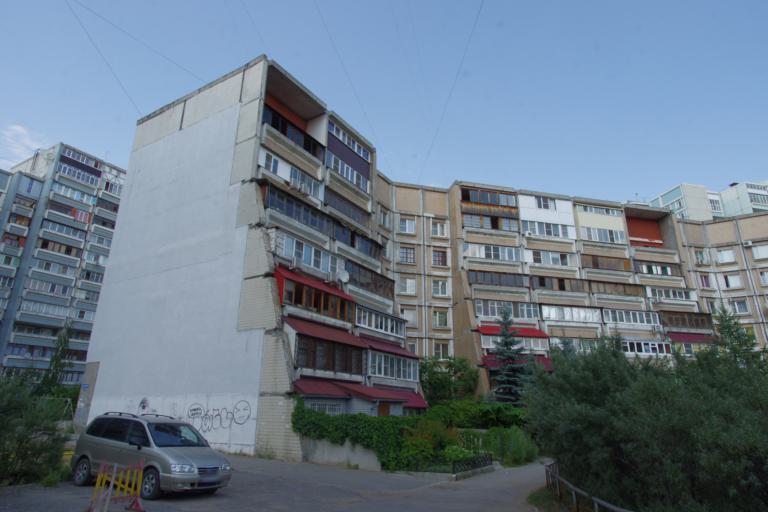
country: RU
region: Nizjnij Novgorod
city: Nizhniy Novgorod
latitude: 56.3434
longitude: 43.9427
